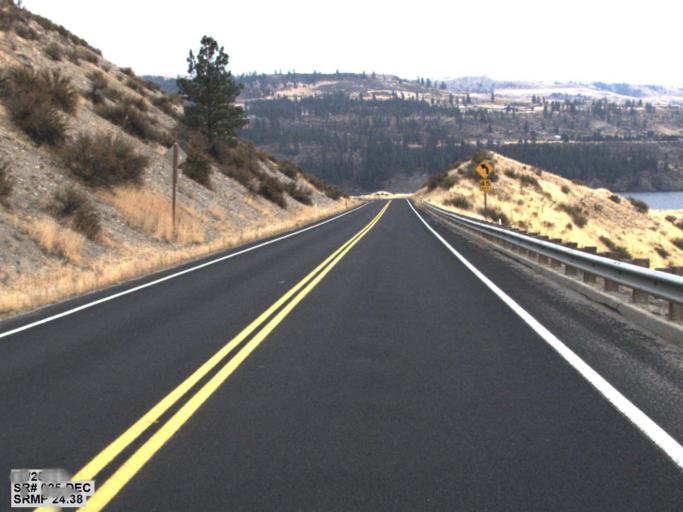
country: US
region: Washington
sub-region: Lincoln County
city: Davenport
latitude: 47.9084
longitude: -118.3353
